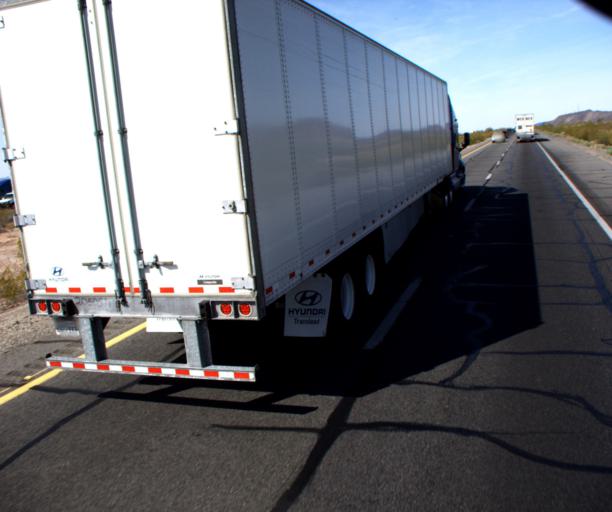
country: US
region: Arizona
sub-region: Maricopa County
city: Buckeye
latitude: 33.5174
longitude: -113.0490
